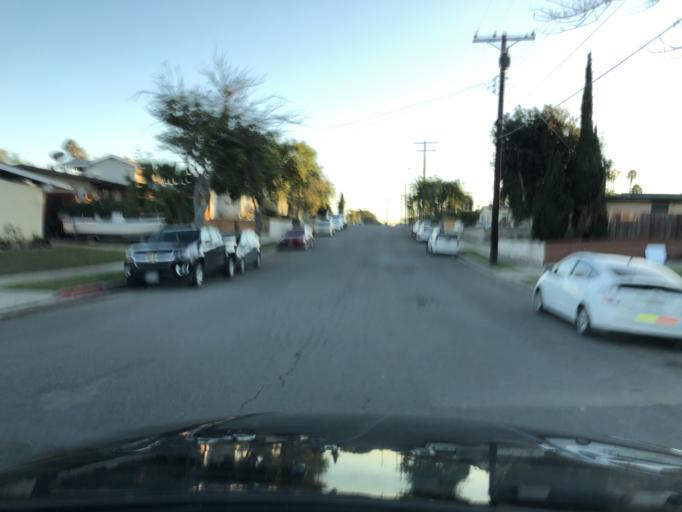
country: US
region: California
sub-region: San Diego County
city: La Jolla
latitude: 32.8335
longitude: -117.1828
